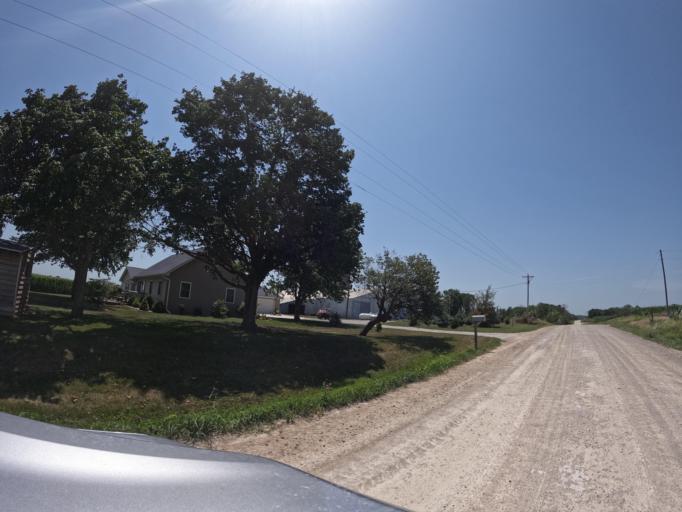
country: US
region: Iowa
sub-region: Henry County
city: Mount Pleasant
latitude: 40.9450
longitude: -91.6566
